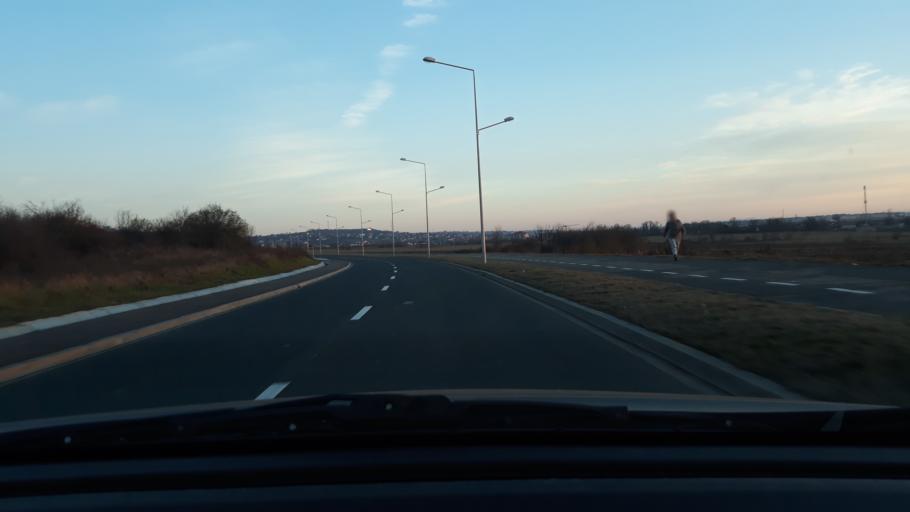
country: RO
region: Bihor
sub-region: Comuna Biharea
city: Oradea
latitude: 47.1035
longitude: 21.9088
